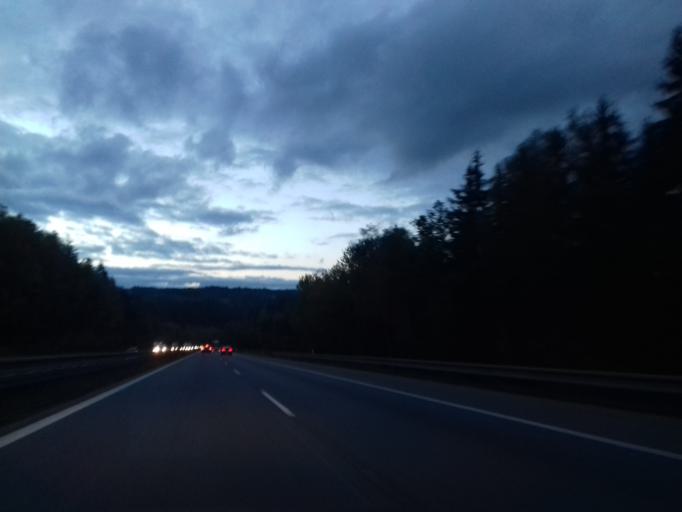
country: CZ
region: Central Bohemia
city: Divisov
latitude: 49.7703
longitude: 14.9445
